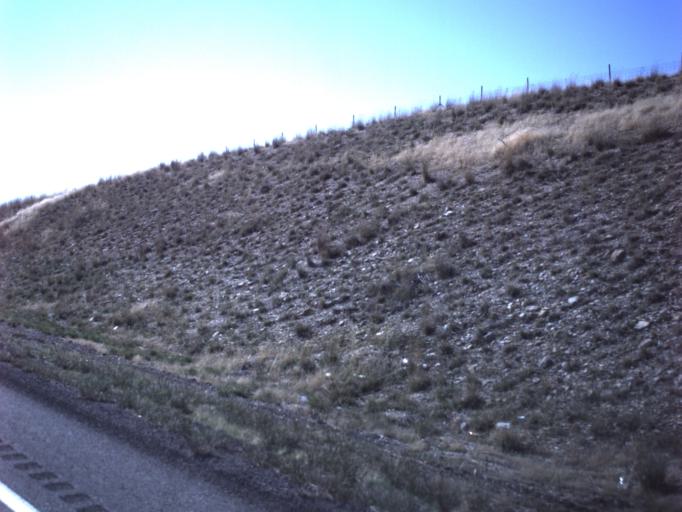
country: US
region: Utah
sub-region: Sanpete County
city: Gunnison
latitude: 39.3353
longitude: -111.9178
